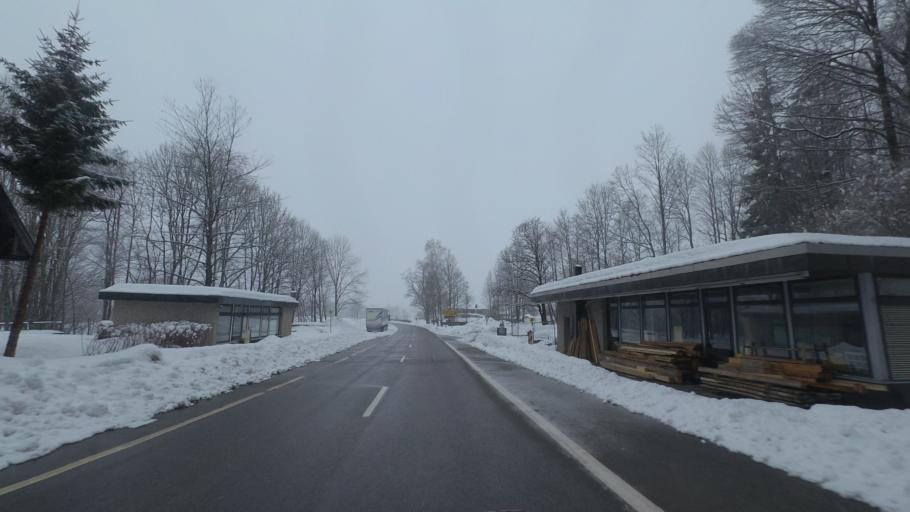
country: DE
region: Bavaria
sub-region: Upper Bavaria
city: Schleching
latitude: 47.7051
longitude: 12.3956
